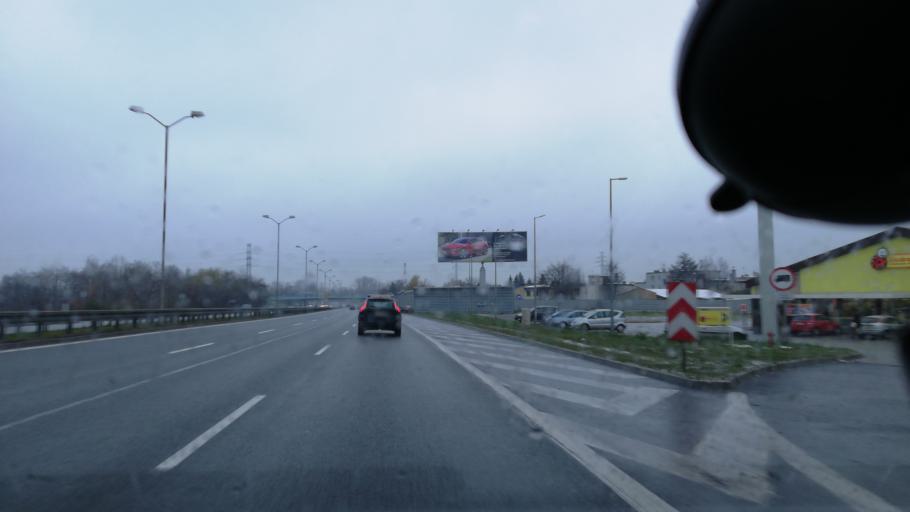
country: PL
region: Silesian Voivodeship
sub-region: Chorzow
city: Chorzow
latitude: 50.2775
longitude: 18.9561
